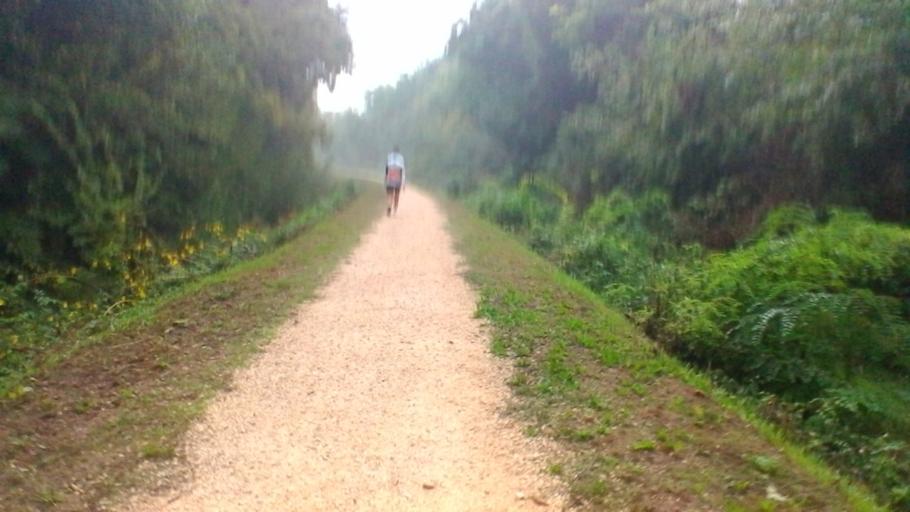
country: IT
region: Veneto
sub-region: Provincia di Verona
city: Verona
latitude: 45.4227
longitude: 10.9999
